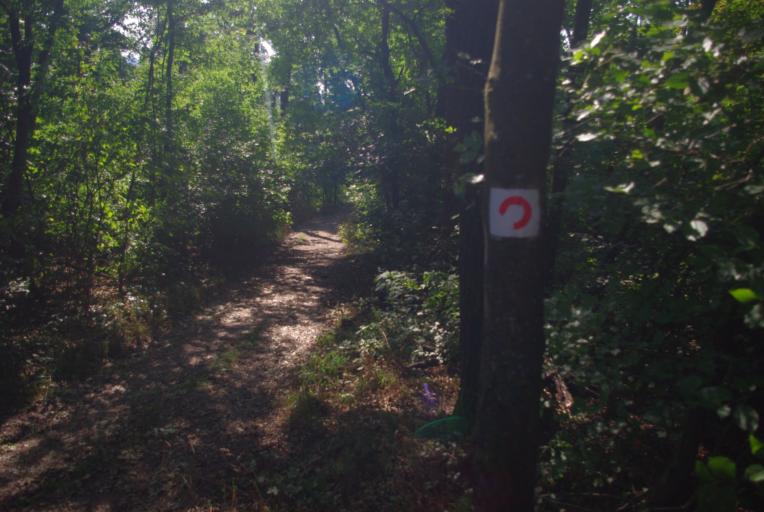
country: HU
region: Budapest
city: Budapest II. keruelet
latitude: 47.5444
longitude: 18.9821
